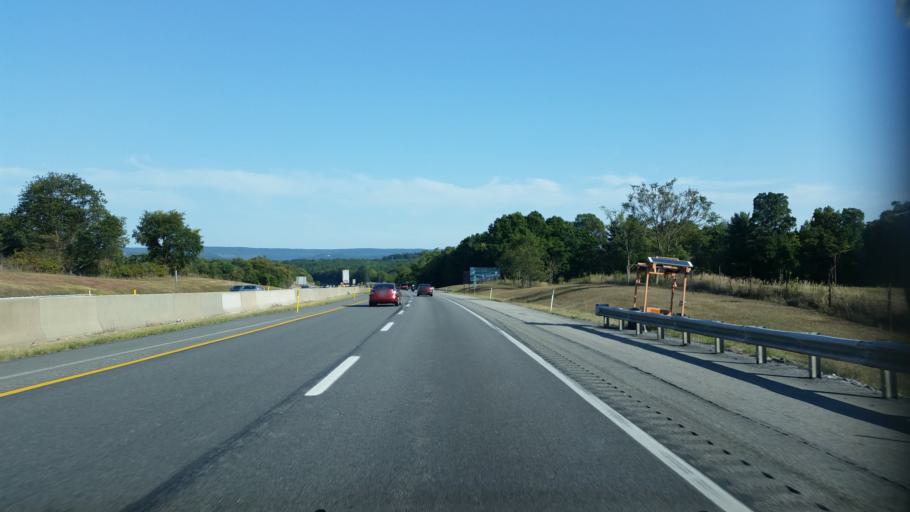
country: US
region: Pennsylvania
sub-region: Fulton County
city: McConnellsburg
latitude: 40.0498
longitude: -78.0685
